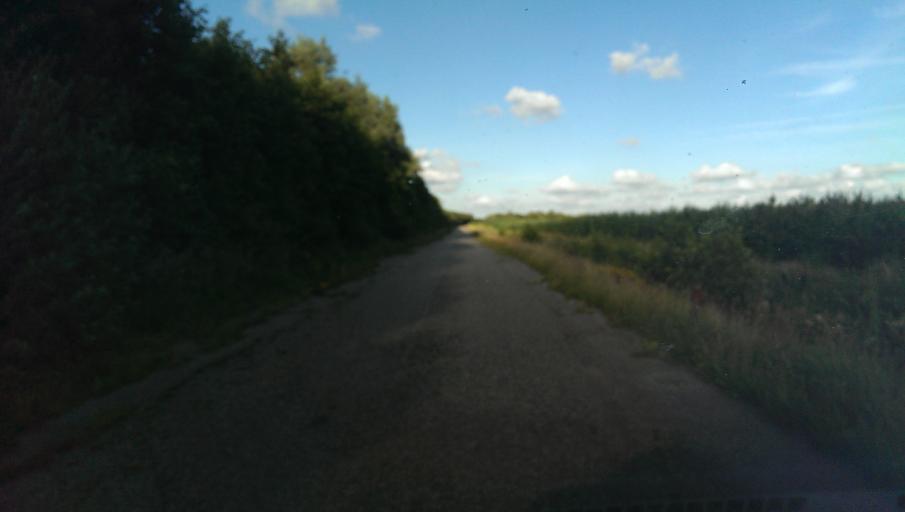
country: DK
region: South Denmark
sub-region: Esbjerg Kommune
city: Tjaereborg
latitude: 55.5230
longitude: 8.5635
